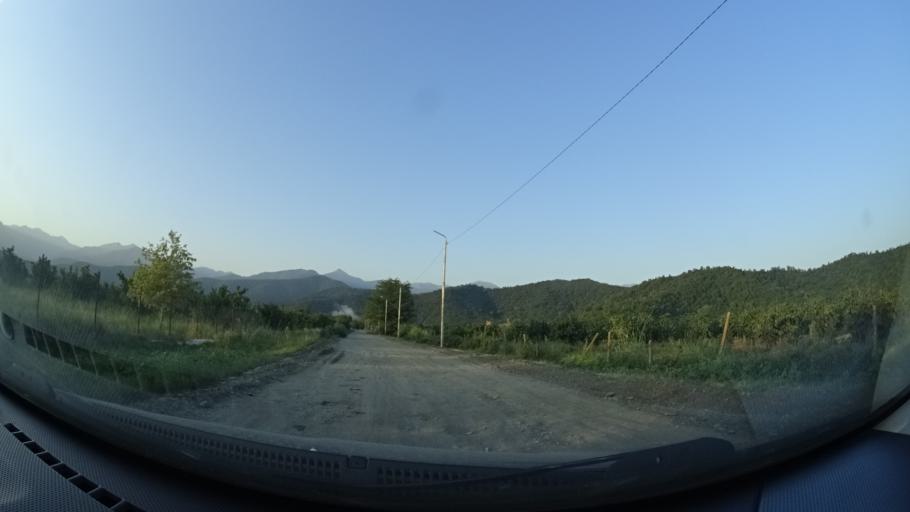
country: GE
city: Bagdadi
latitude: 41.8647
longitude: 46.0170
